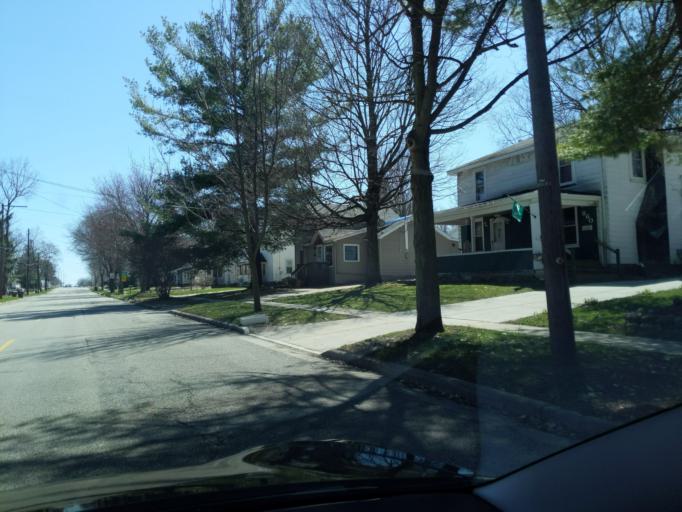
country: US
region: Michigan
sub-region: Ingham County
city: Mason
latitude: 42.5737
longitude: -84.4400
